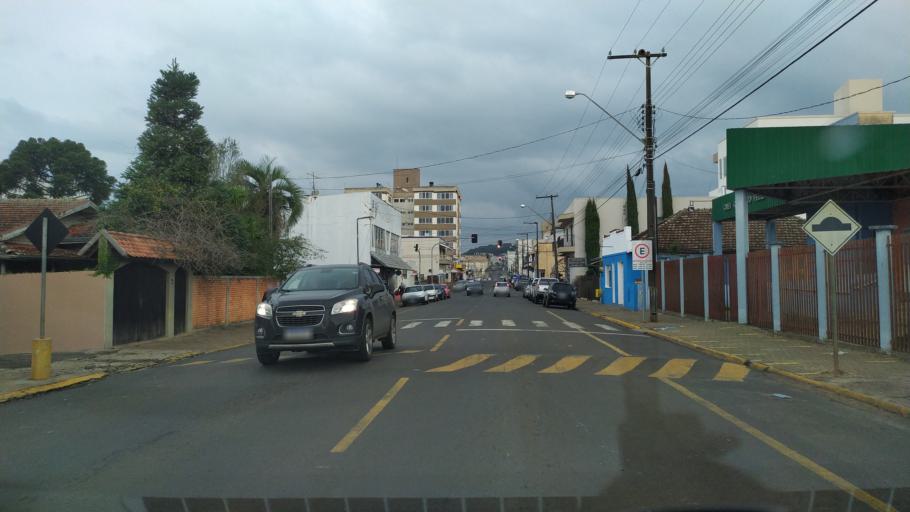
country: BR
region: Parana
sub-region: Palmas
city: Palmas
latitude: -26.4814
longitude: -51.9941
